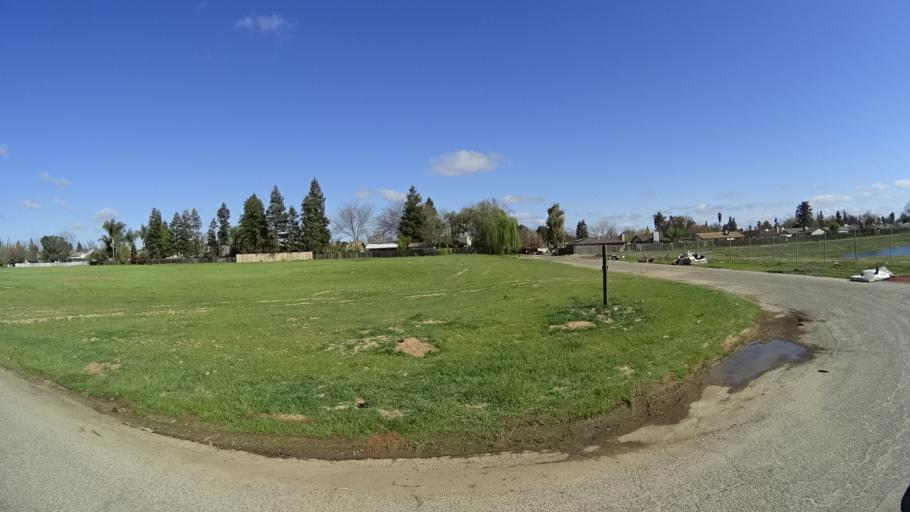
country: US
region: California
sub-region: Fresno County
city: West Park
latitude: 36.7946
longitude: -119.8874
